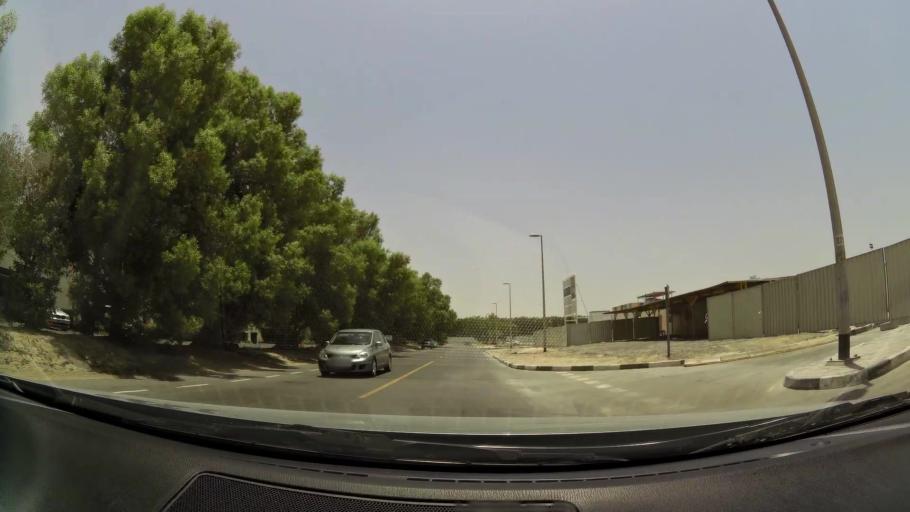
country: AE
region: Dubai
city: Dubai
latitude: 25.1784
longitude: 55.2429
